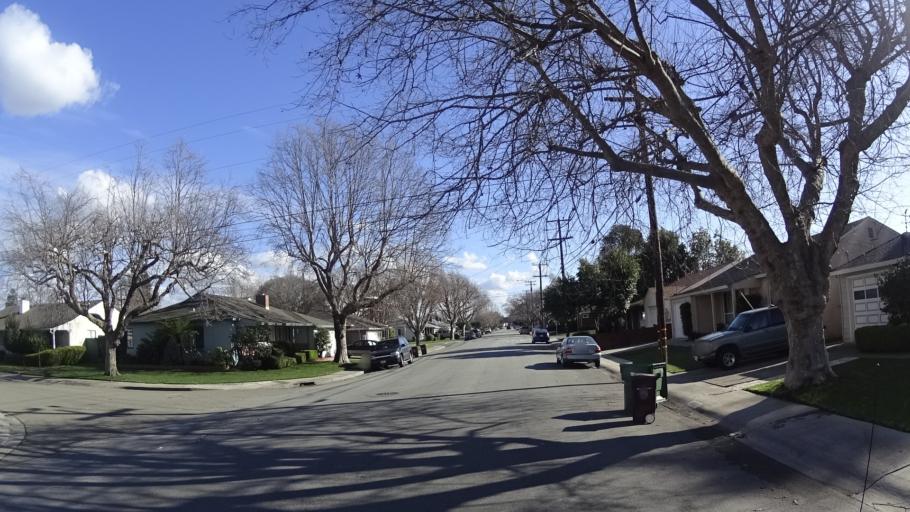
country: US
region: California
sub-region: Alameda County
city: San Lorenzo
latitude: 37.6815
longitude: -122.1205
